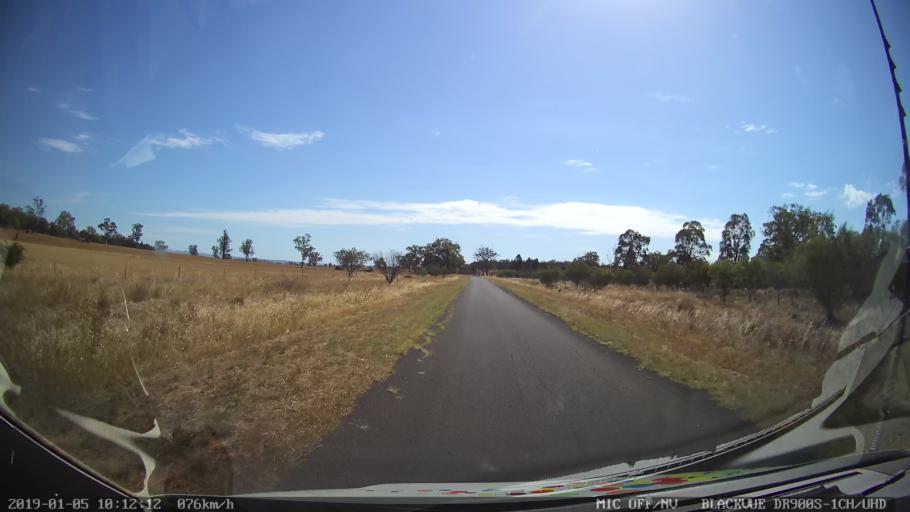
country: AU
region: New South Wales
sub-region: Gilgandra
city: Gilgandra
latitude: -31.6092
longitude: 148.9103
